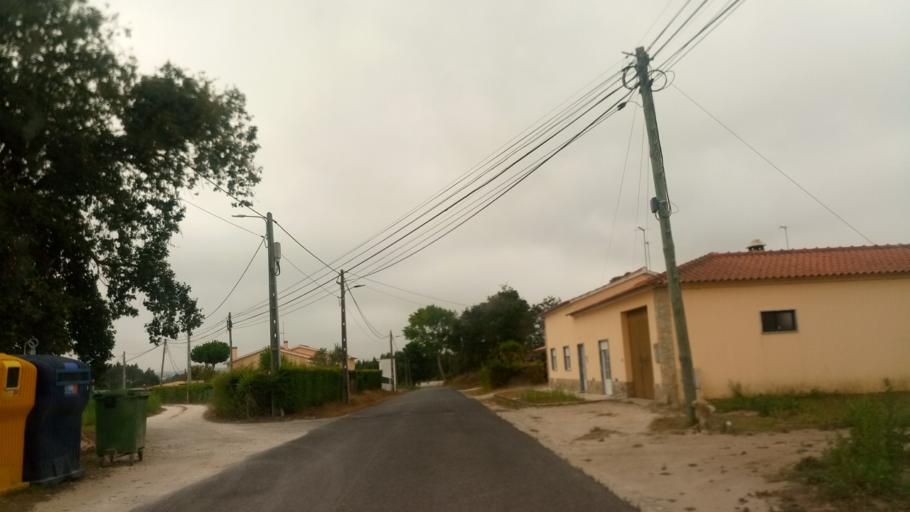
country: PT
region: Leiria
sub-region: Caldas da Rainha
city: Caldas da Rainha
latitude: 39.4187
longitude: -9.1456
